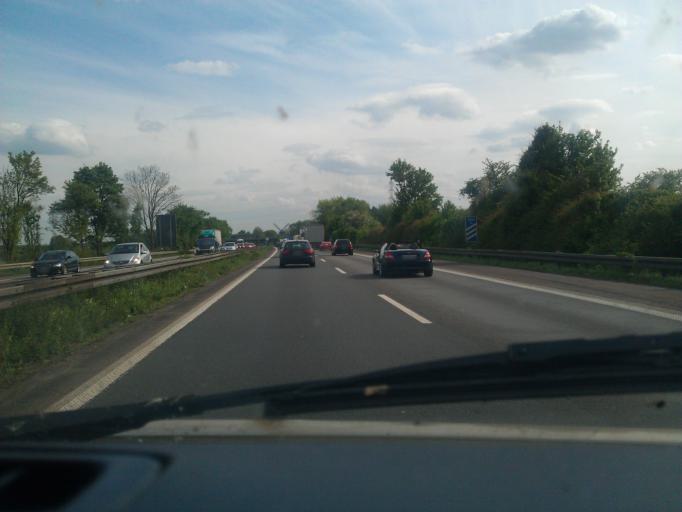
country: DE
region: North Rhine-Westphalia
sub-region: Regierungsbezirk Dusseldorf
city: Krefeld
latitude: 51.3187
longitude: 6.6313
